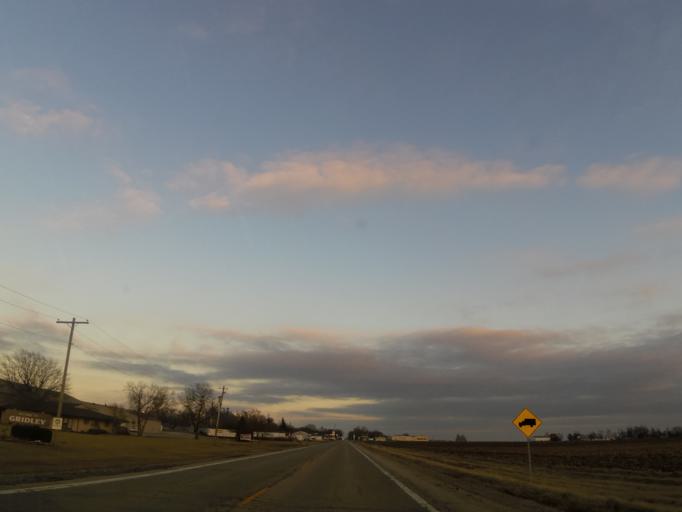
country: US
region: Illinois
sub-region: McLean County
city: Gridley
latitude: 40.7396
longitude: -88.8903
